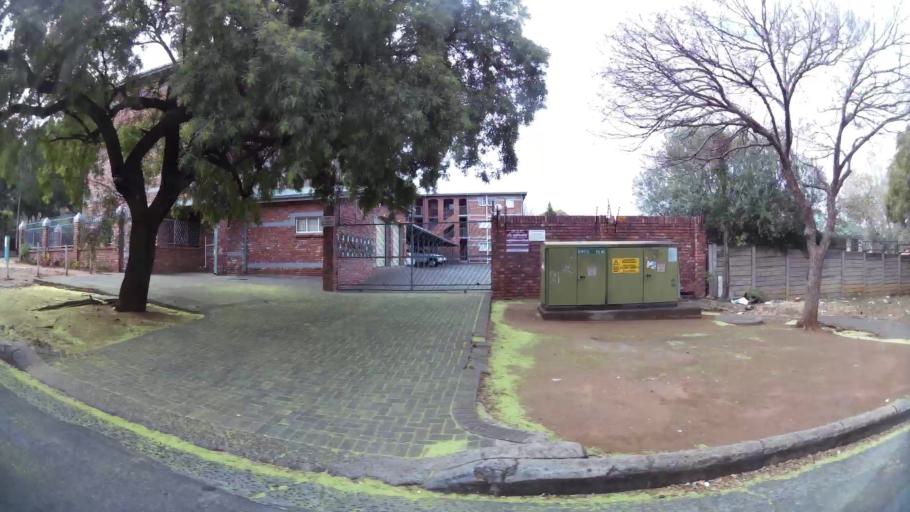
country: ZA
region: Orange Free State
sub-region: Mangaung Metropolitan Municipality
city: Bloemfontein
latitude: -29.1092
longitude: 26.2278
